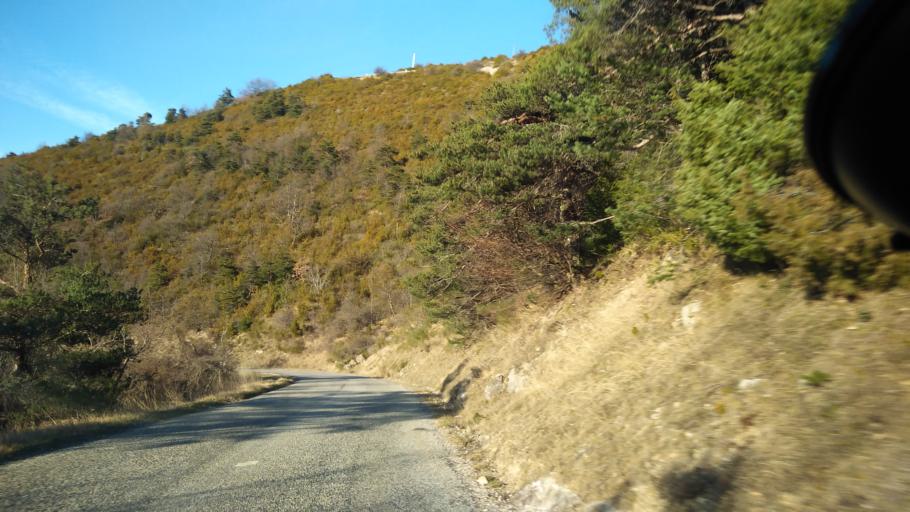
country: FR
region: Rhone-Alpes
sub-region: Departement de la Drome
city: Chabeuil
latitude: 44.8472
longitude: 5.0893
